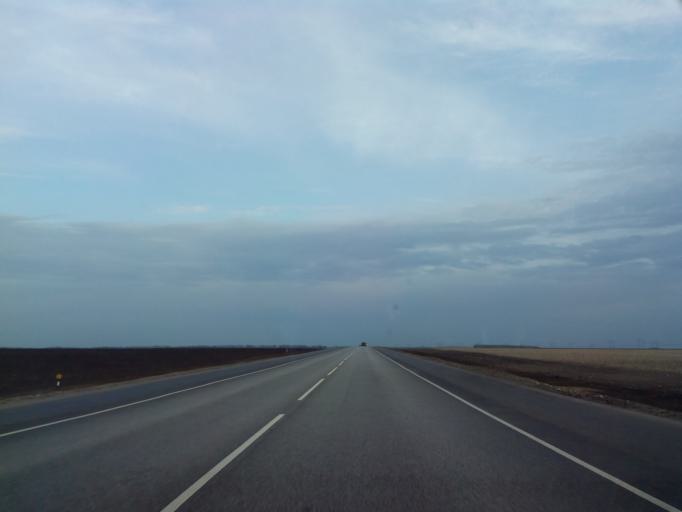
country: RU
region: Rjazan
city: Ryazhsk
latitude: 53.5745
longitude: 40.0452
